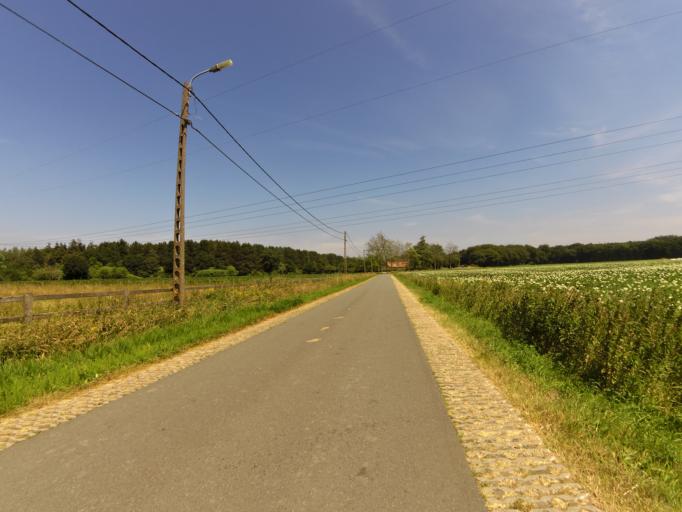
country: BE
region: Flanders
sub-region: Provincie West-Vlaanderen
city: Zedelgem
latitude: 51.1731
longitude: 3.1330
